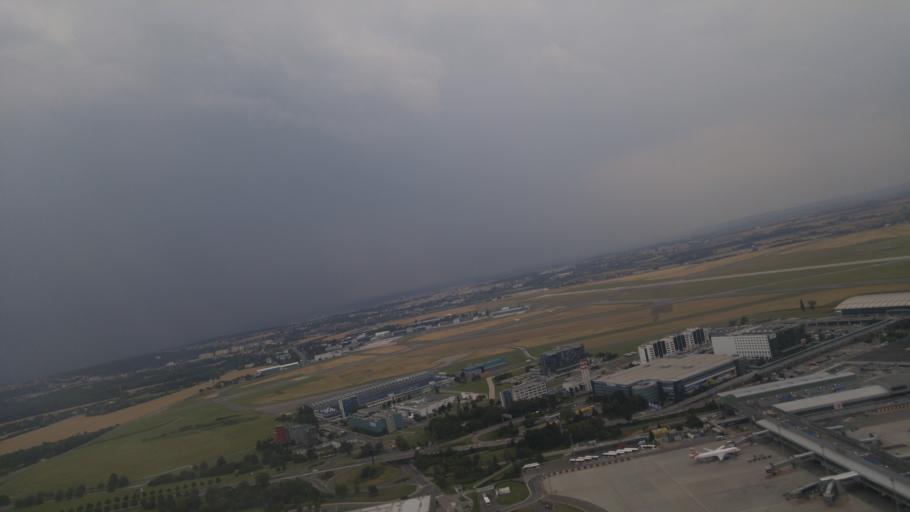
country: CZ
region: Central Bohemia
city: Tuchomerice
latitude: 50.1152
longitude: 14.2695
